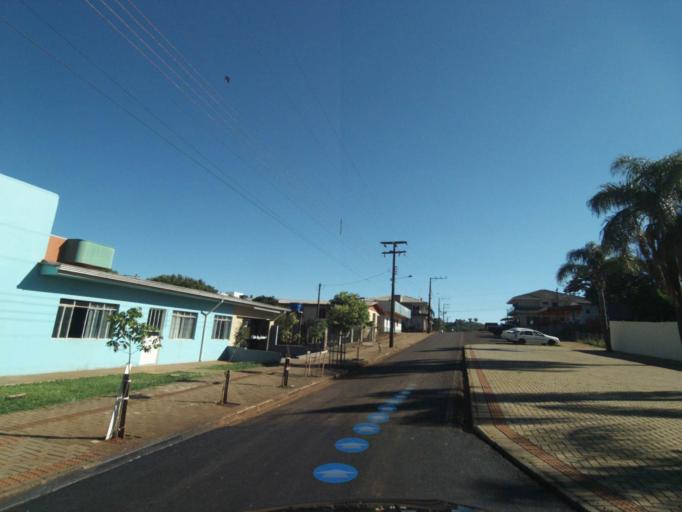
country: BR
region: Parana
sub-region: Coronel Vivida
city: Coronel Vivida
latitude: -26.1425
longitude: -52.3863
